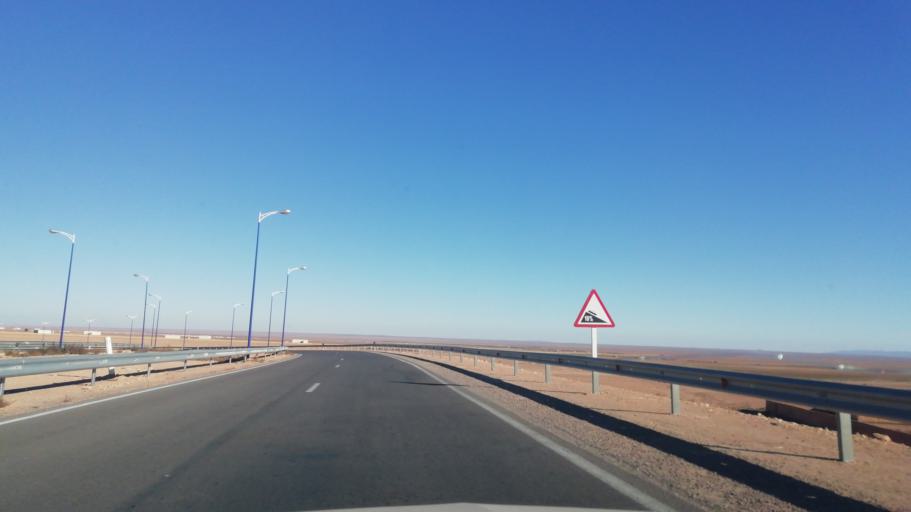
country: DZ
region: Wilaya de Naama
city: Naama
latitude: 33.5127
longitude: -0.2805
